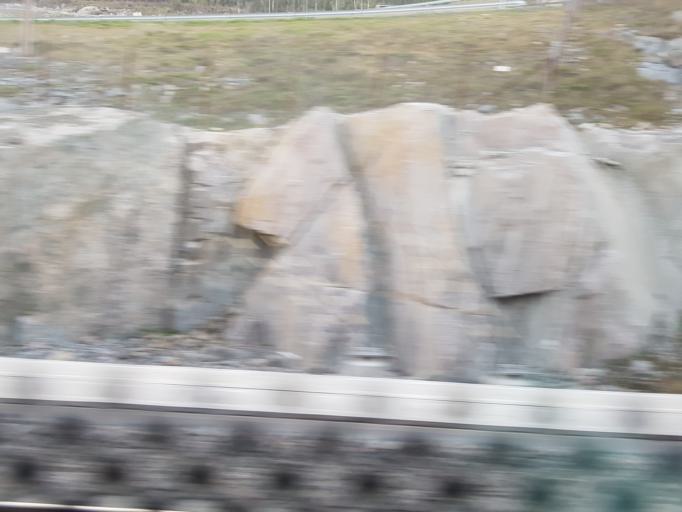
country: NO
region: Akershus
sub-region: Eidsvoll
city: Eidsvoll
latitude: 60.4835
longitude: 11.2367
